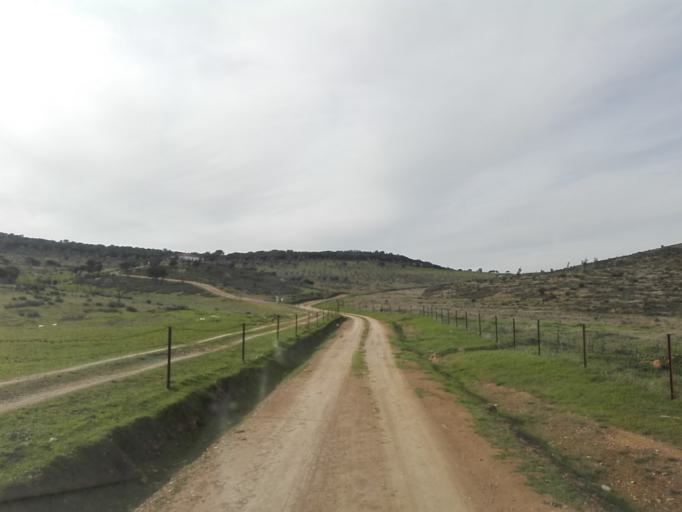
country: ES
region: Extremadura
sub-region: Provincia de Badajoz
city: Llerena
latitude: 38.2168
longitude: -6.0354
